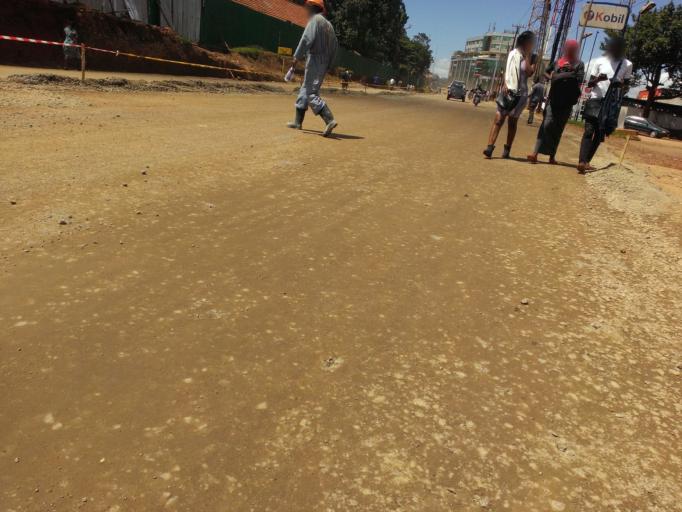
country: UG
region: Central Region
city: Kampala Central Division
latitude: 0.3277
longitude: 32.5678
